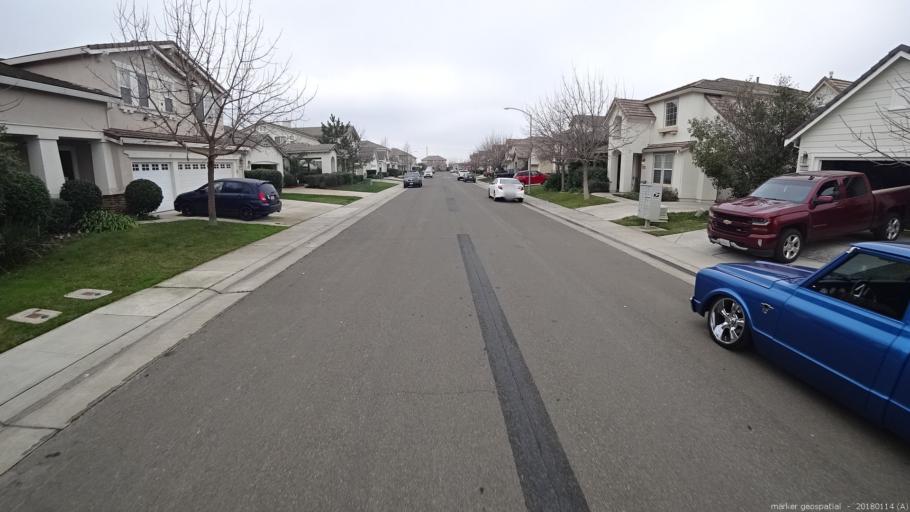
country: US
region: California
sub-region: Sacramento County
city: Rancho Cordova
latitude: 38.5524
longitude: -121.2402
